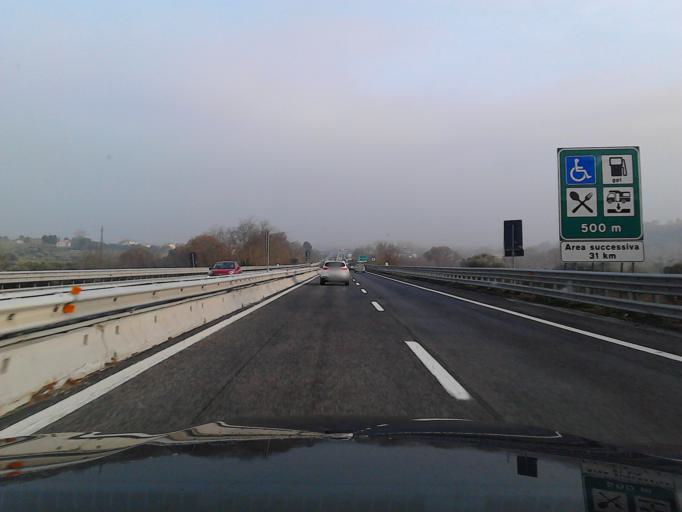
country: IT
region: Abruzzo
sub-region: Provincia di Pescara
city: Fonte Umano-San Martino Alta
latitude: 42.5331
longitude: 14.1168
